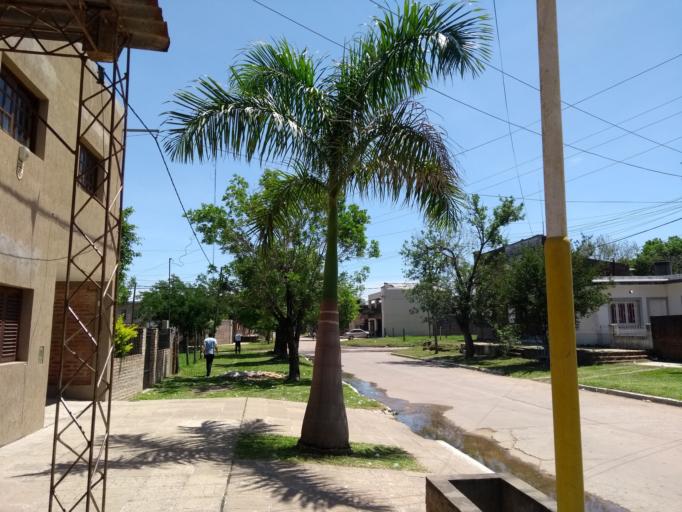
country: AR
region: Chaco
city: Barranqueras
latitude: -27.4871
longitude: -58.9295
